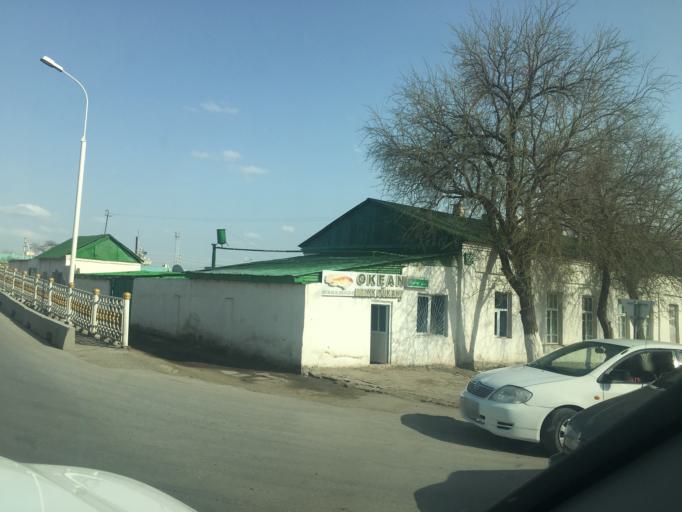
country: TM
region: Lebap
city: Turkmenabat
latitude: 39.0940
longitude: 63.5665
